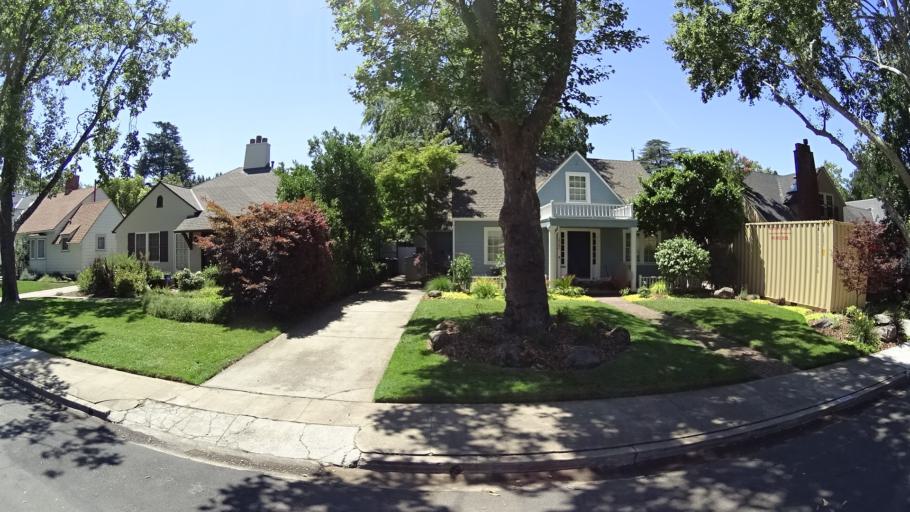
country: US
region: California
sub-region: Sacramento County
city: Sacramento
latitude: 38.5481
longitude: -121.4776
